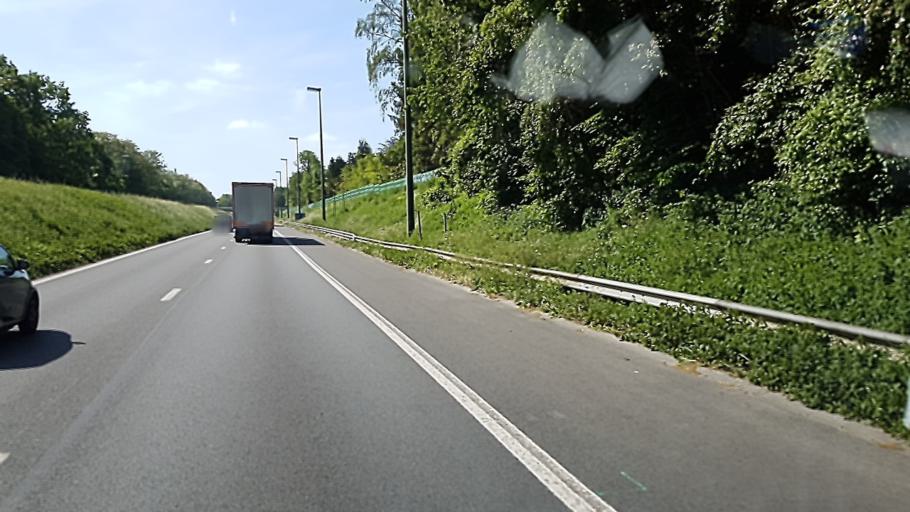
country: BE
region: Wallonia
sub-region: Province du Brabant Wallon
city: Waterloo
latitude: 50.6996
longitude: 4.4126
